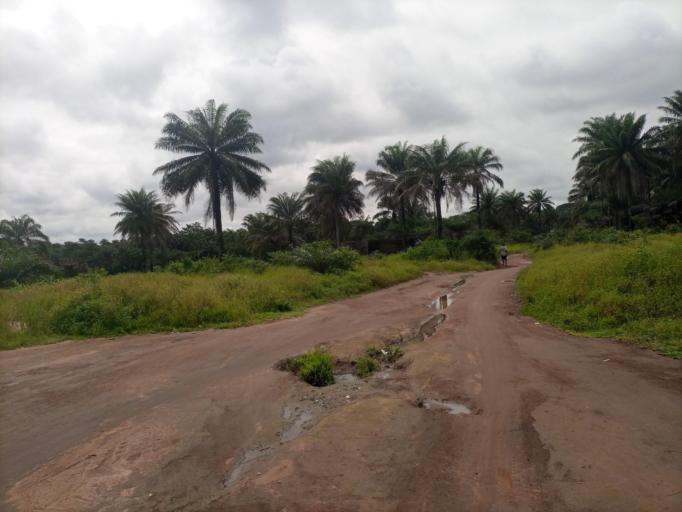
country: SL
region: Northern Province
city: Sawkta
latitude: 8.6250
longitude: -13.1966
